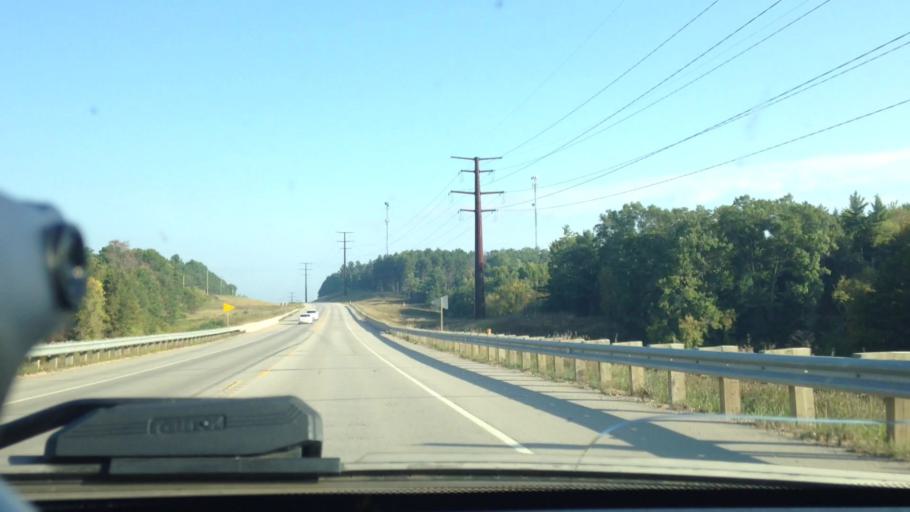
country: US
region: Wisconsin
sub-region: Marinette County
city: Peshtigo
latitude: 45.2079
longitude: -87.9944
